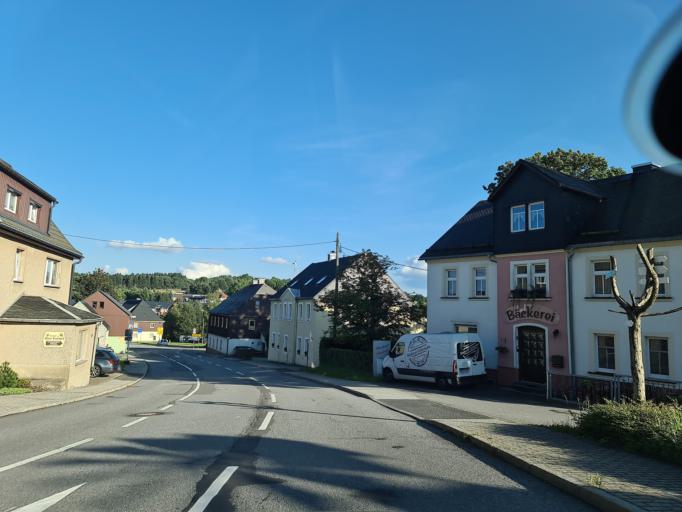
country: DE
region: Saxony
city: Deutschneudorf
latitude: 50.6314
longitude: 13.4933
